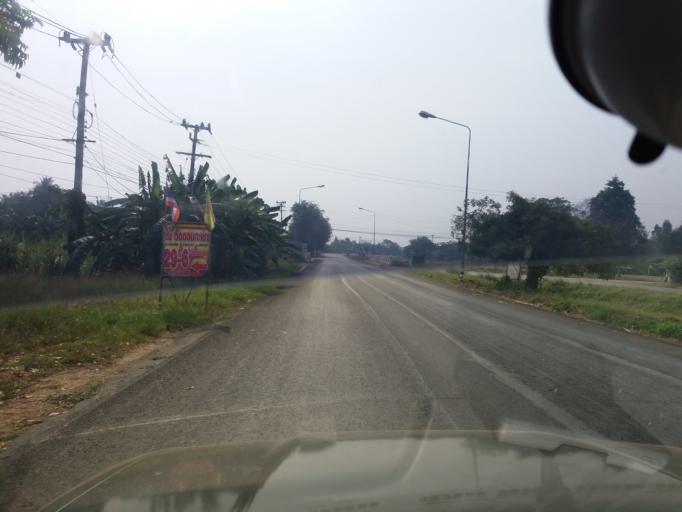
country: TH
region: Sing Buri
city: Bang Racham
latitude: 14.9041
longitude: 100.2240
